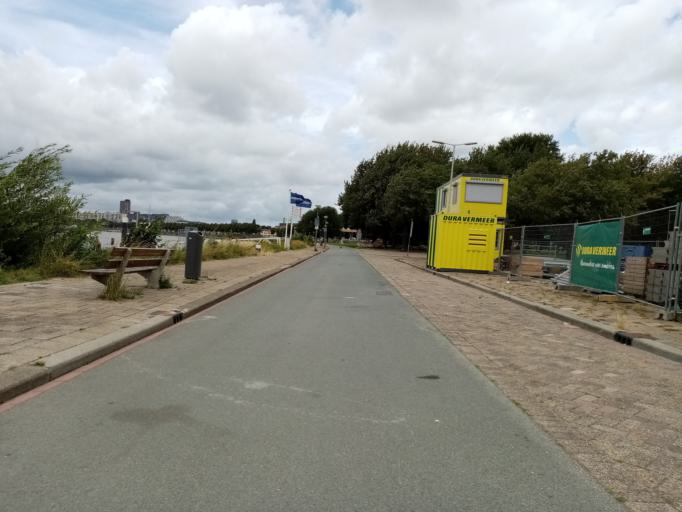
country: NL
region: South Holland
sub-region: Gemeente Rotterdam
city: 's-Gravenland
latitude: 51.9128
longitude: 4.5179
